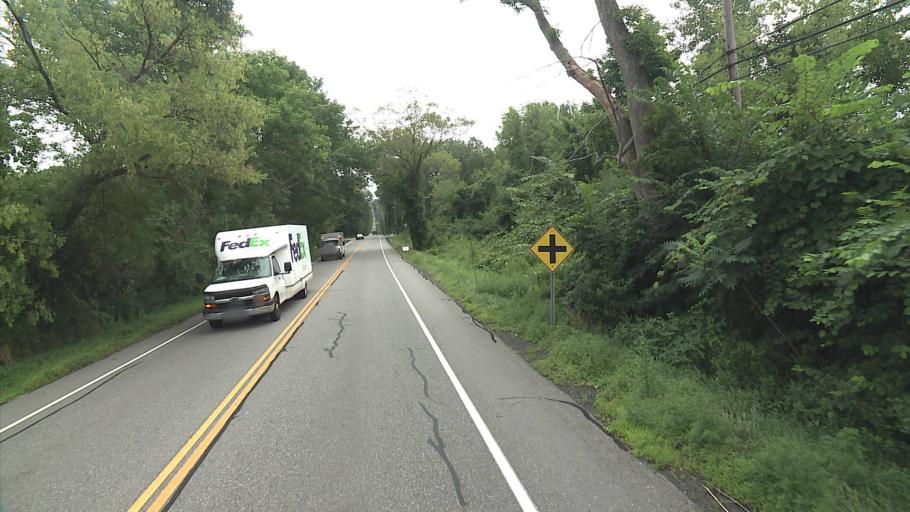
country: US
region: Connecticut
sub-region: Tolland County
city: Storrs
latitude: 41.8700
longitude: -72.2087
